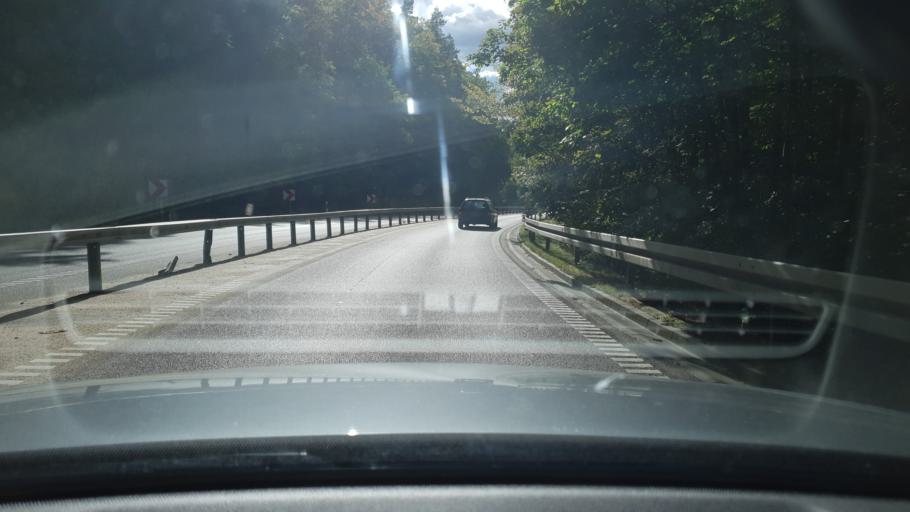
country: PL
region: Pomeranian Voivodeship
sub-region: Powiat wejherowski
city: Rekowo Dolne
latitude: 54.6278
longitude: 18.3435
